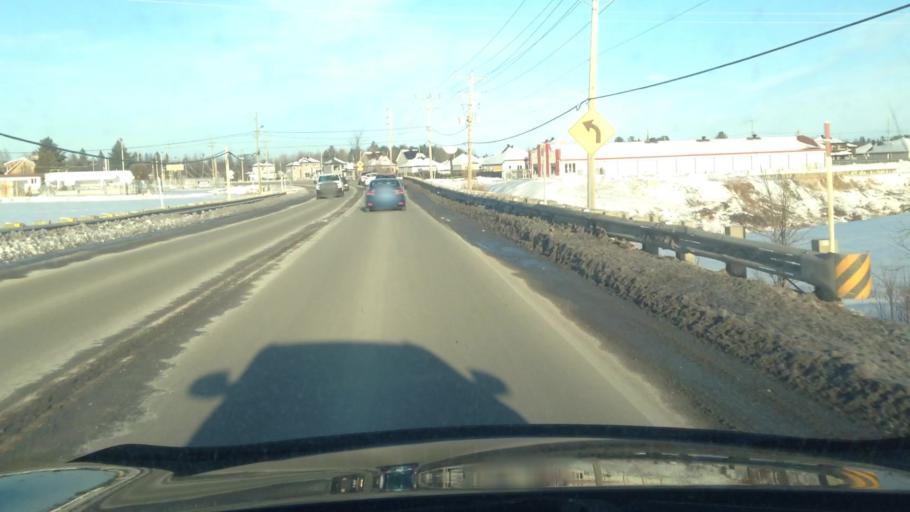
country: CA
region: Quebec
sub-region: Laurentides
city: Sainte-Sophie
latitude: 45.8249
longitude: -73.8884
